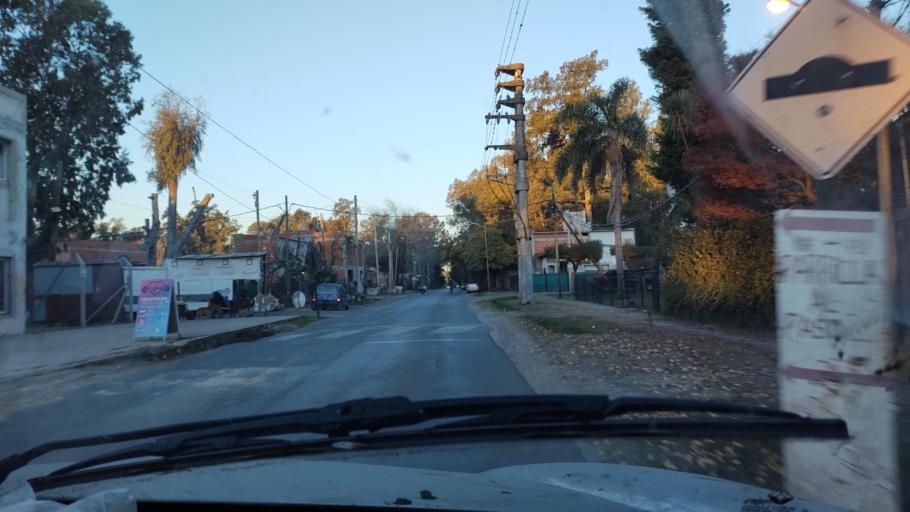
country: AR
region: Buenos Aires
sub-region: Partido de La Plata
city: La Plata
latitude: -34.9031
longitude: -58.0492
